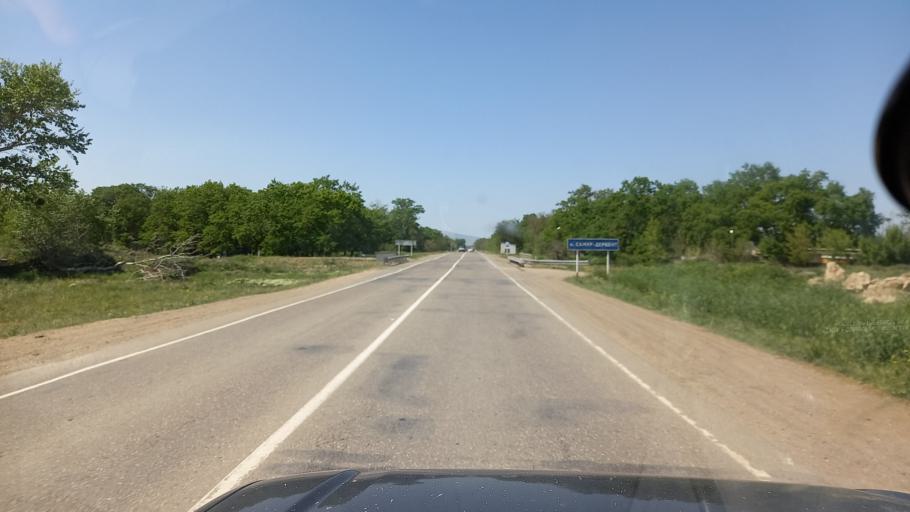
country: RU
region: Dagestan
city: Belidzhi
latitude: 41.8379
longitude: 48.3821
